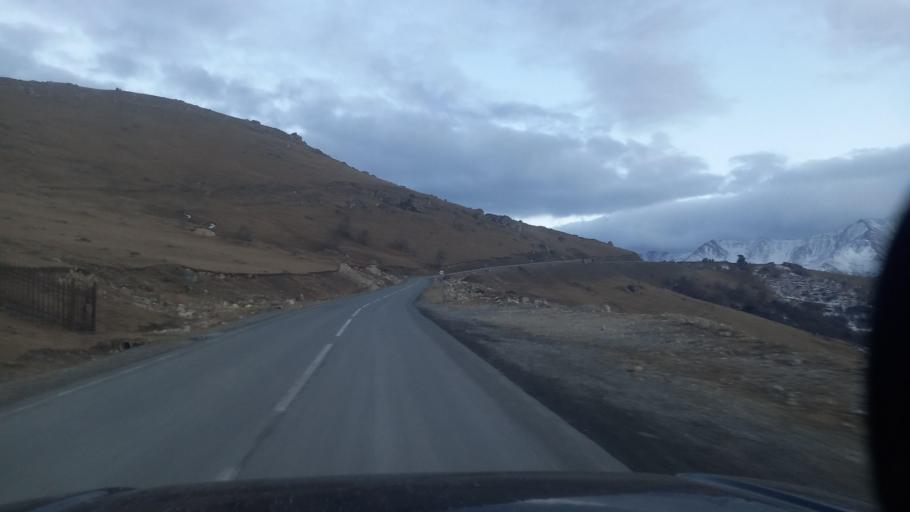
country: RU
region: Ingushetiya
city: Dzhayrakh
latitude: 42.8249
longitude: 44.8249
